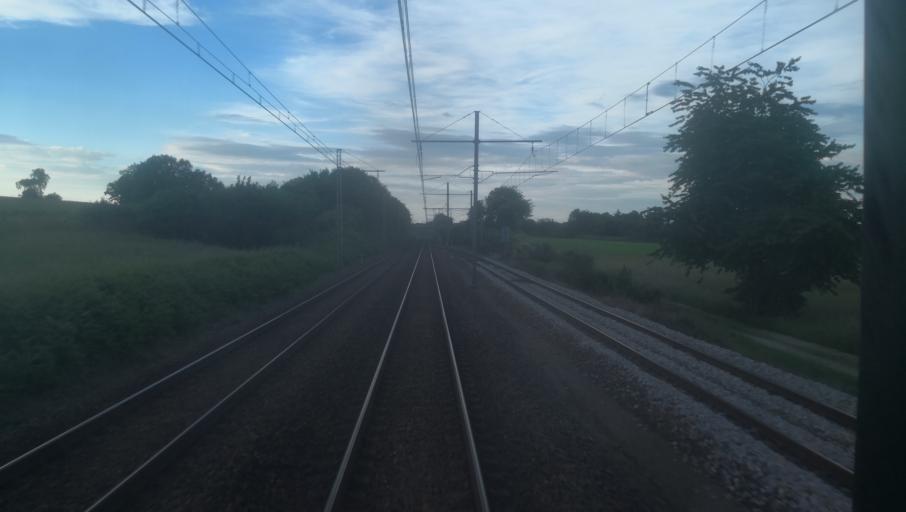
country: FR
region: Limousin
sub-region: Departement de la Creuse
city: Saint-Agnant-de-Versillat
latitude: 46.3209
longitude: 1.5259
